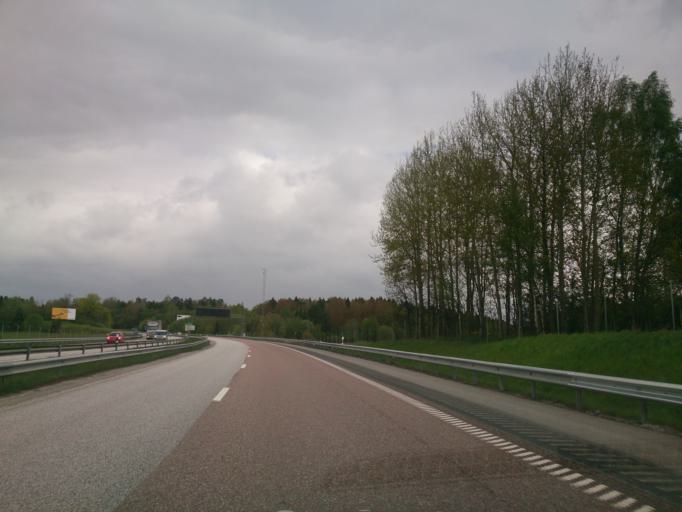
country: SE
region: Stockholm
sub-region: Sodertalje Kommun
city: Pershagen
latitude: 59.1435
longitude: 17.6499
